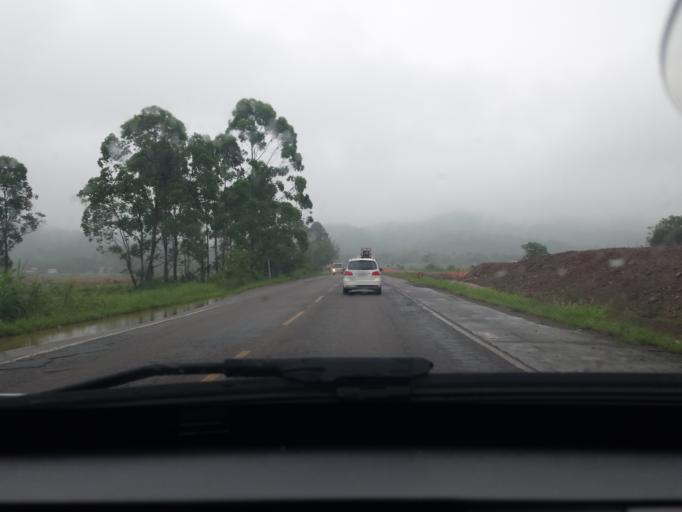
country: BR
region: Santa Catarina
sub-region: Itajai
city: Itajai
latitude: -26.8346
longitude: -48.7528
